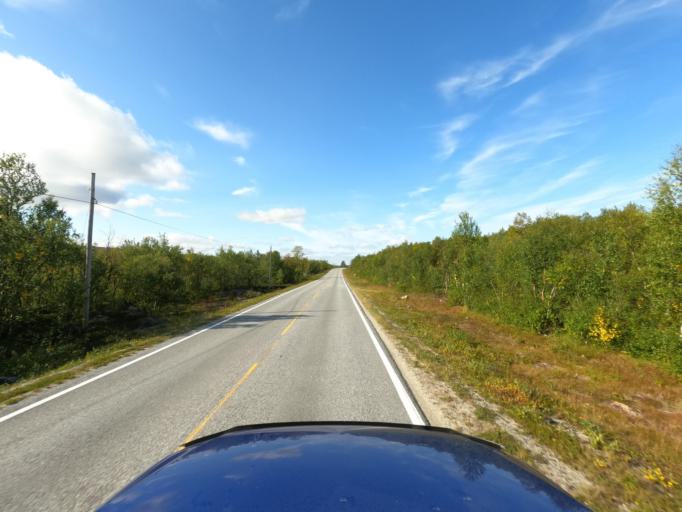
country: NO
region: Finnmark Fylke
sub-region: Porsanger
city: Lakselv
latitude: 69.7643
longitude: 25.1864
